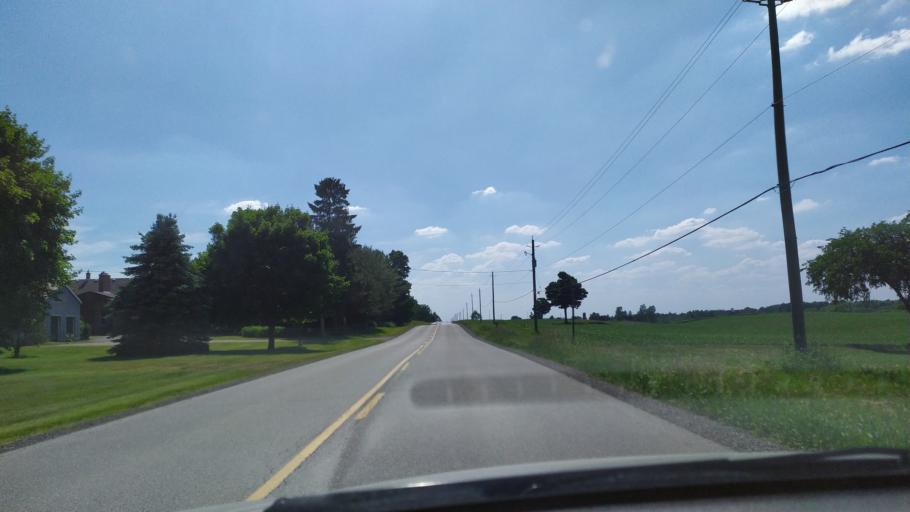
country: CA
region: Ontario
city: Kitchener
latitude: 43.3655
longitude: -80.5965
